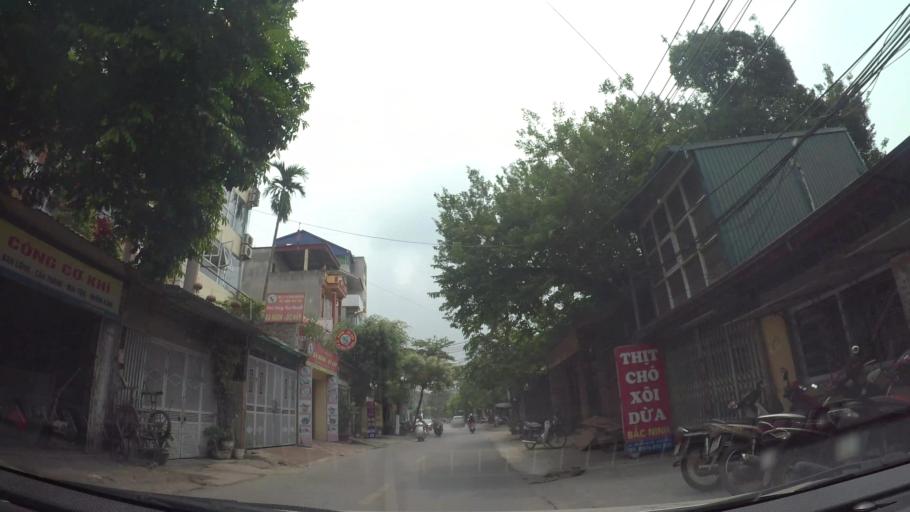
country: VN
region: Ha Noi
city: Ha Dong
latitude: 20.9708
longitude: 105.7661
